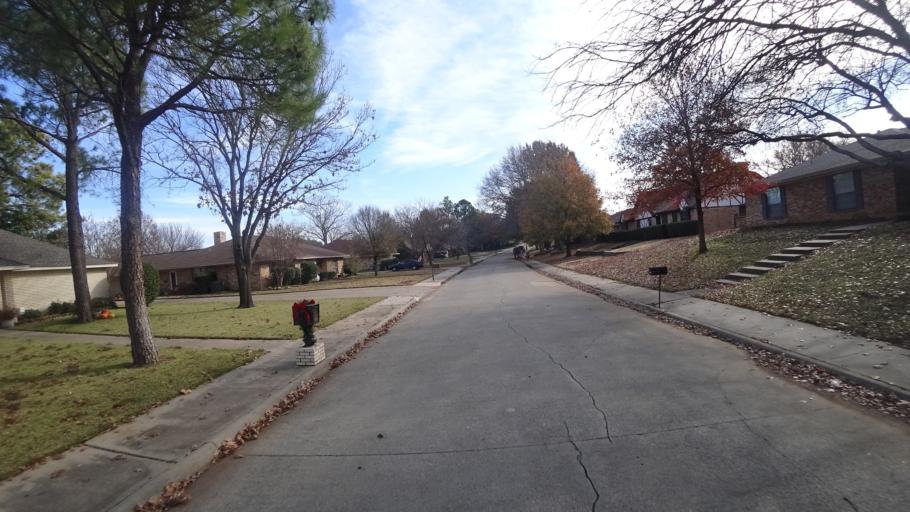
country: US
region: Texas
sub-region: Denton County
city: Lewisville
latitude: 33.0525
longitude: -97.0305
